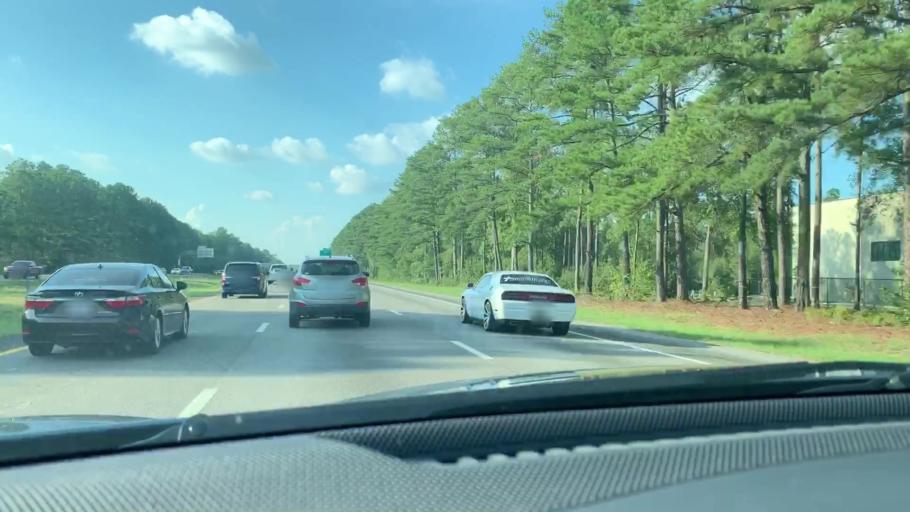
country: US
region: South Carolina
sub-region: Lexington County
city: Pineridge
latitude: 33.8950
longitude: -81.0440
